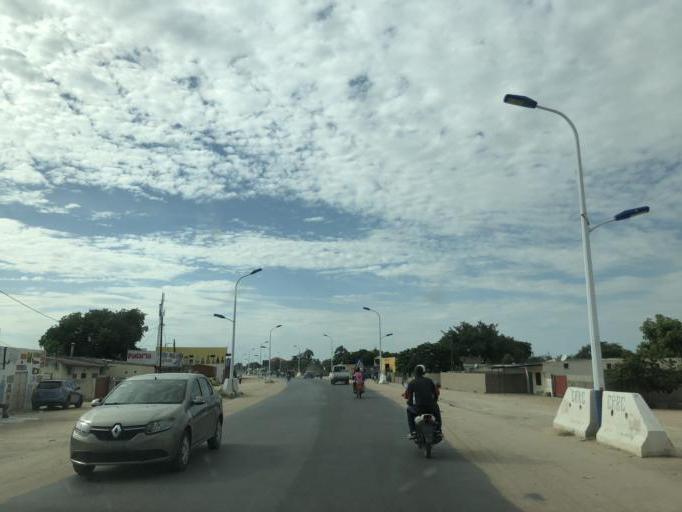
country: AO
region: Cunene
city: Ondjiva
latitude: -17.0735
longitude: 15.7331
